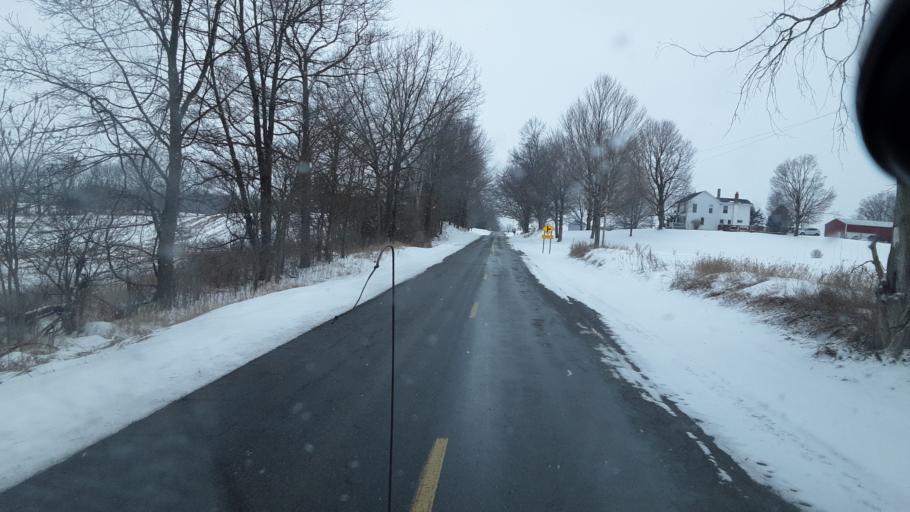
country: US
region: Michigan
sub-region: Ingham County
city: Leslie
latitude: 42.4367
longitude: -84.4597
